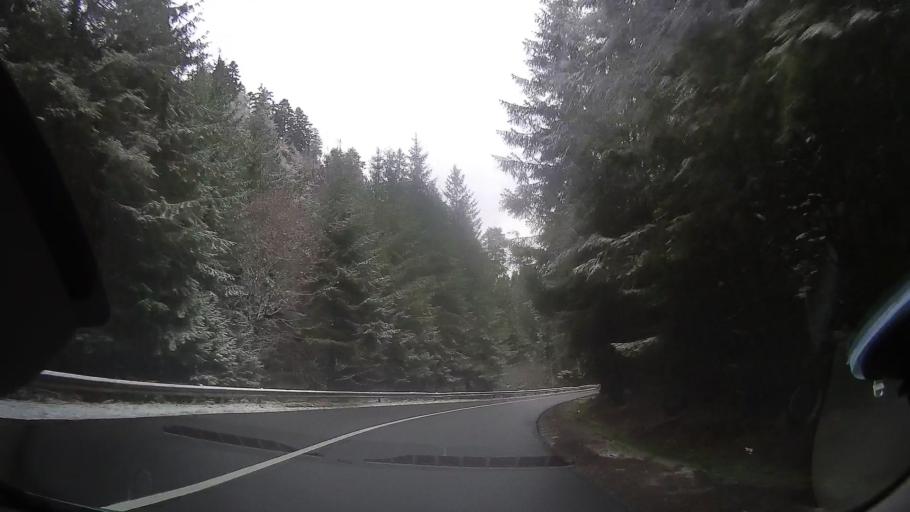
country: RO
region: Cluj
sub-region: Comuna Calatele
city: Calatele
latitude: 46.7368
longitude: 23.0387
